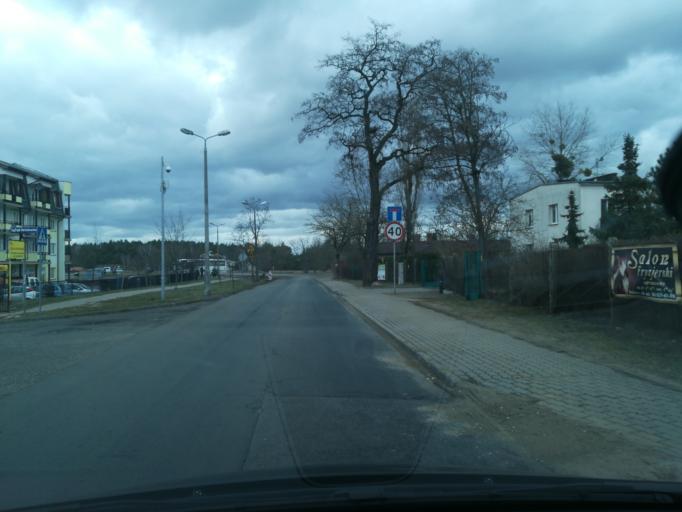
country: PL
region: Kujawsko-Pomorskie
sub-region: Powiat torunski
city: Lubicz Dolny
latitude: 52.9823
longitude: 18.6854
